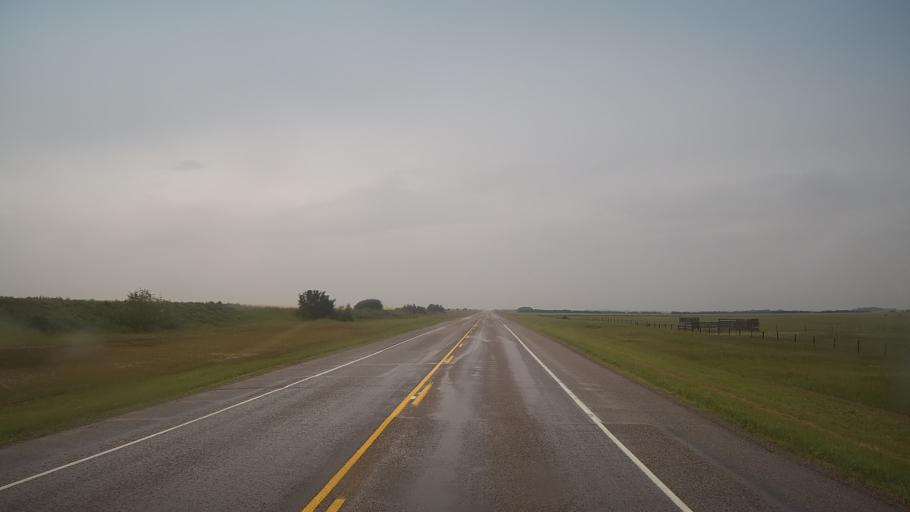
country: CA
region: Saskatchewan
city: Wilkie
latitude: 52.2180
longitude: -108.5089
